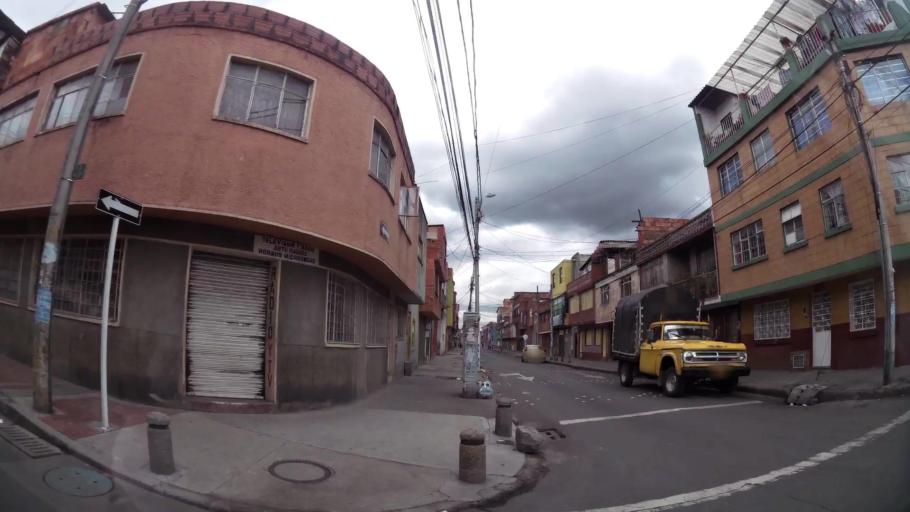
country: CO
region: Bogota D.C.
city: Barrio San Luis
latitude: 4.6880
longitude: -74.0857
